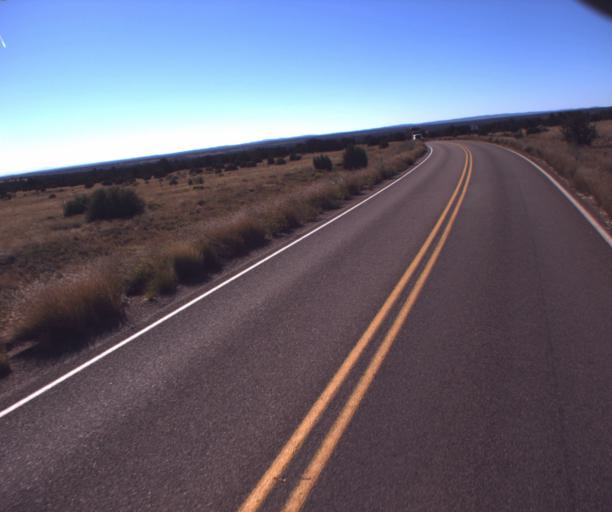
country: US
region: Arizona
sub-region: Navajo County
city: Heber-Overgaard
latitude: 34.4842
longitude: -110.3405
